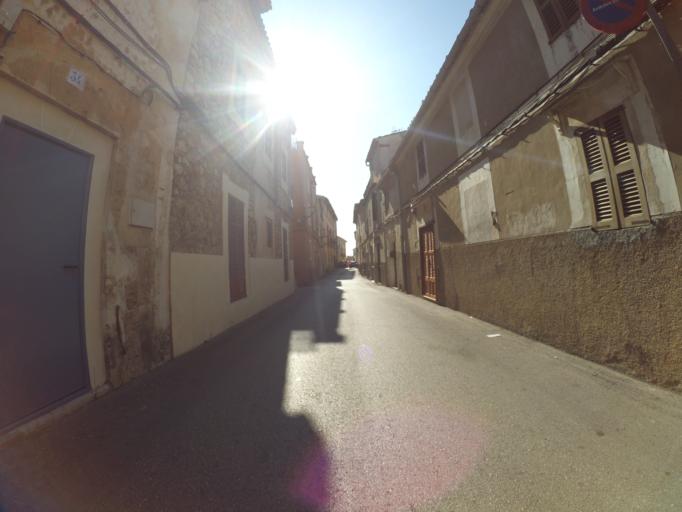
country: ES
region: Balearic Islands
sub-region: Illes Balears
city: Arta
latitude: 39.6954
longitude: 3.3496
